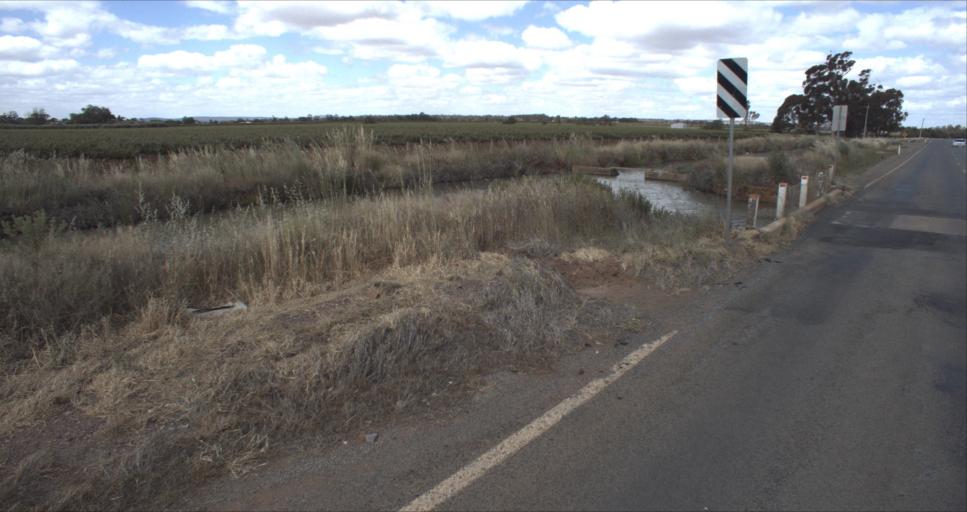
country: AU
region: New South Wales
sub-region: Leeton
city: Leeton
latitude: -34.5787
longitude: 146.3980
